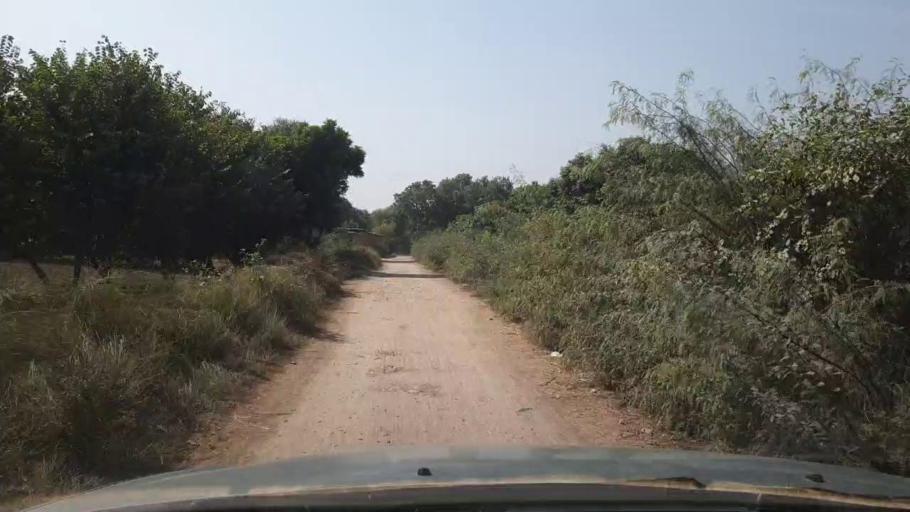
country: PK
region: Sindh
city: Tando Jam
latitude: 25.3727
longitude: 68.5347
